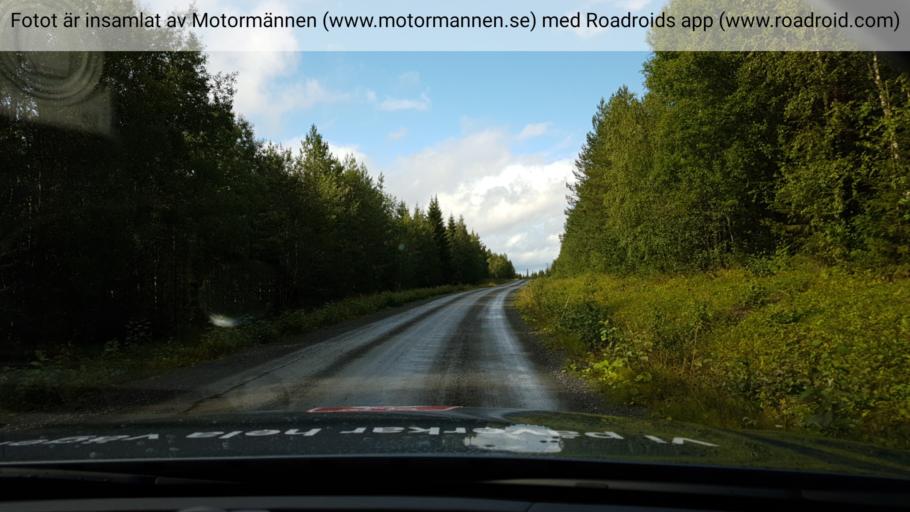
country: SE
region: Jaemtland
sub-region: Krokoms Kommun
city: Krokom
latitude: 63.7094
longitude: 14.5259
